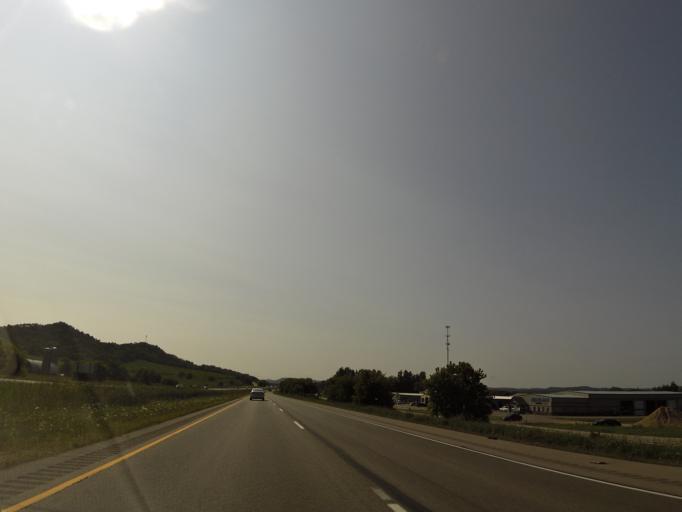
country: US
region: Wisconsin
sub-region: La Crosse County
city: West Salem
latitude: 43.8915
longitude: -91.0558
